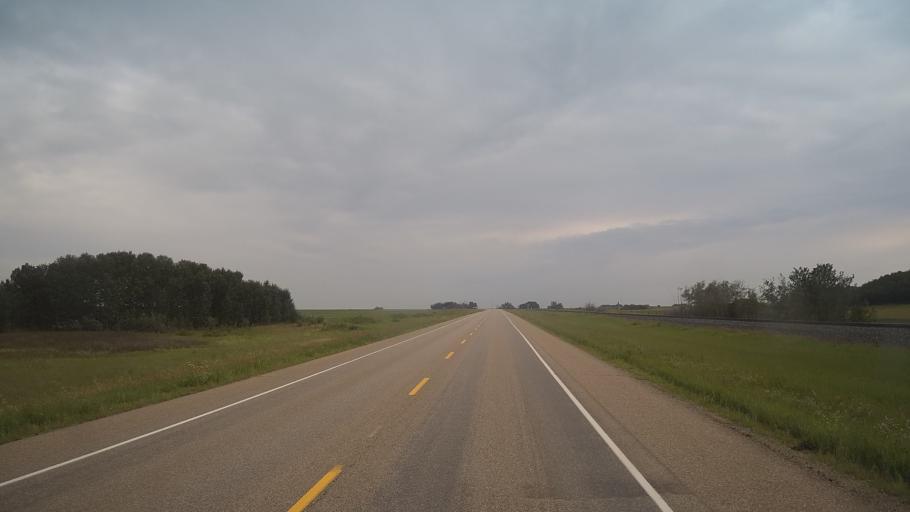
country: CA
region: Saskatchewan
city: Langham
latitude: 52.1266
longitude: -107.2776
